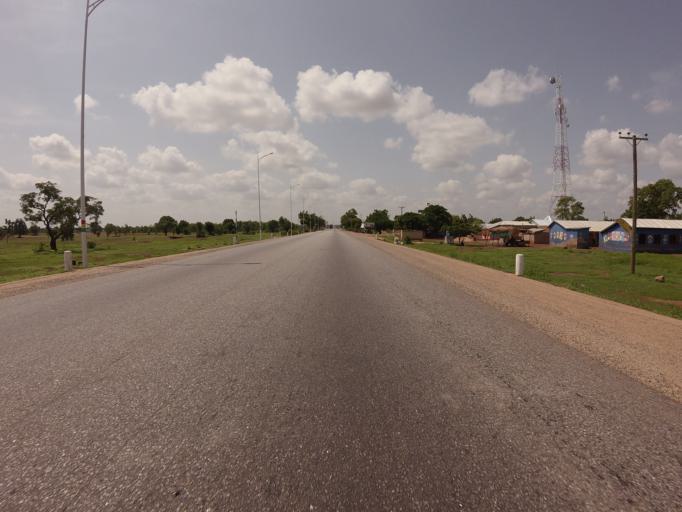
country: GH
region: Northern
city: Savelugu
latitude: 9.5459
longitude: -0.8383
